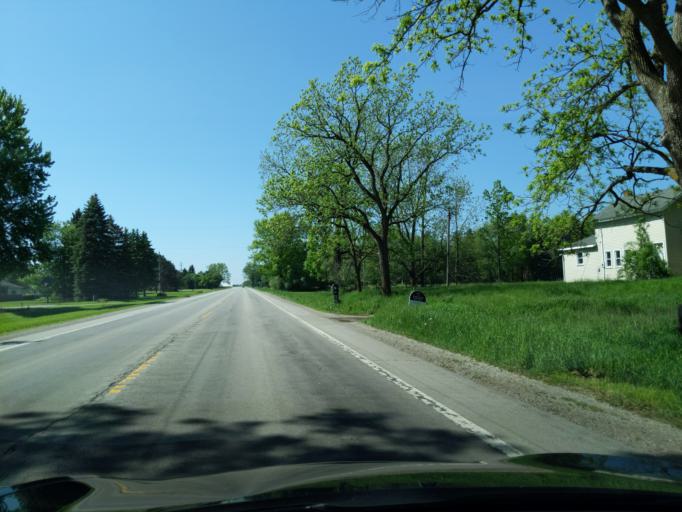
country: US
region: Michigan
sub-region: Ingham County
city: Stockbridge
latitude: 42.4728
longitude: -84.1901
